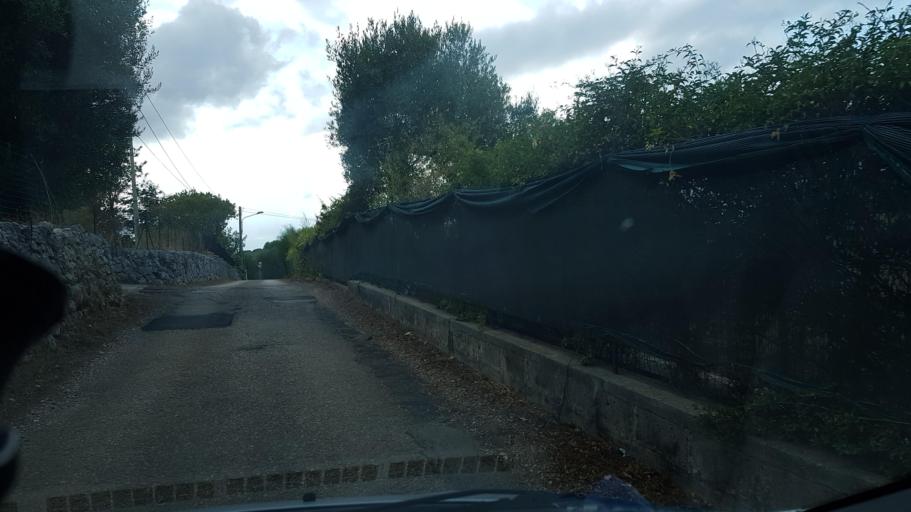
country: IT
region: Apulia
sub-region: Provincia di Brindisi
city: San Vito dei Normanni
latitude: 40.6674
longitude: 17.7209
